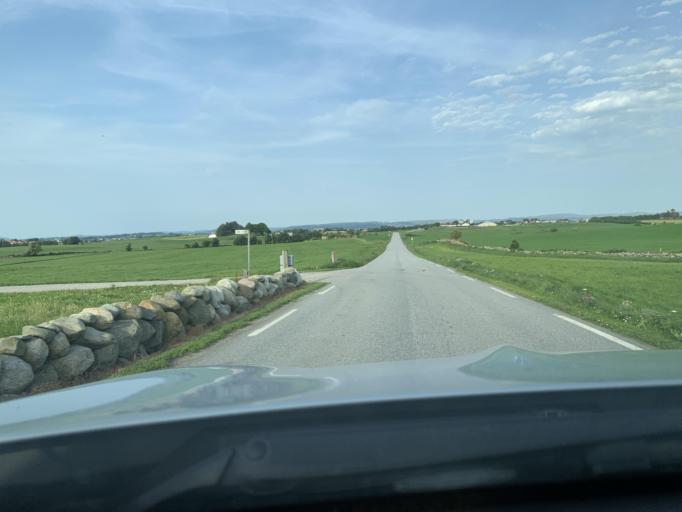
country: NO
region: Rogaland
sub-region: Klepp
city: Kleppe
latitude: 58.7179
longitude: 5.5469
